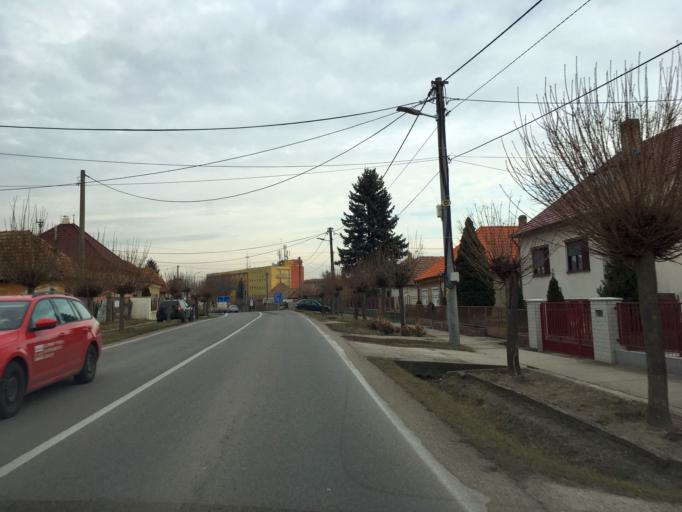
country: SK
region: Nitriansky
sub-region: Okres Nove Zamky
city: Nove Zamky
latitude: 47.9944
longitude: 18.2608
